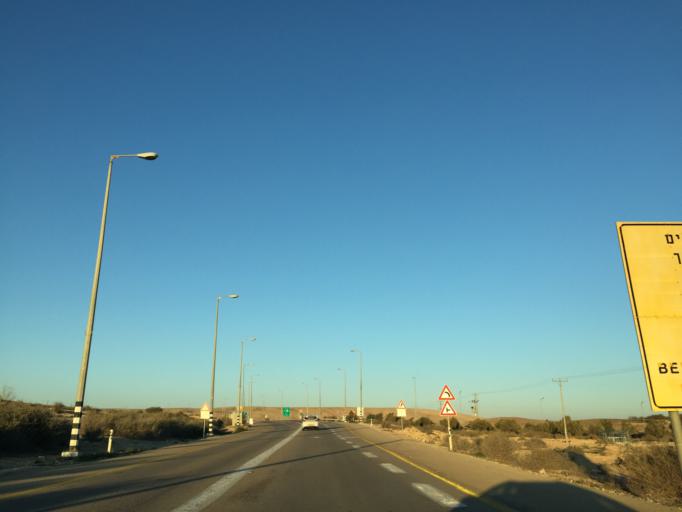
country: IL
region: Southern District
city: Midreshet Ben-Gurion
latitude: 30.8788
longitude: 34.7911
